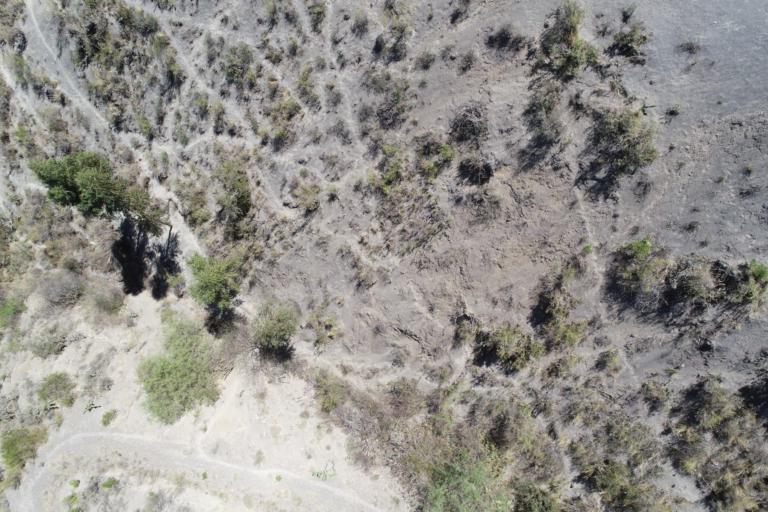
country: BO
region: La Paz
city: La Paz
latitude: -16.6270
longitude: -68.0504
